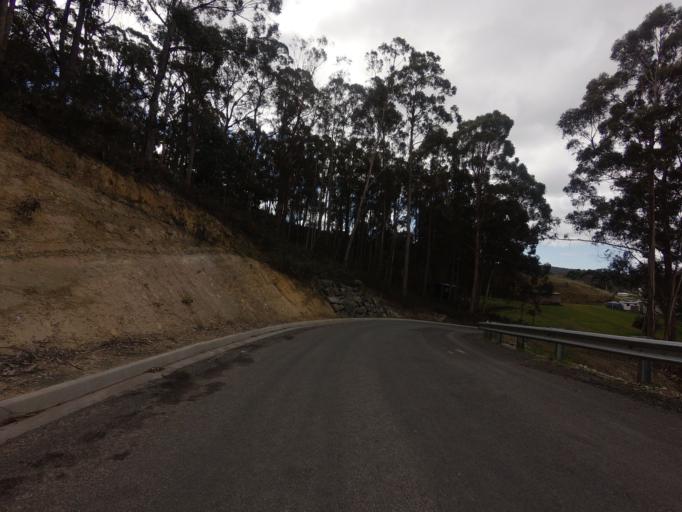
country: AU
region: Tasmania
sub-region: Huon Valley
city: Geeveston
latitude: -43.4338
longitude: 146.9667
